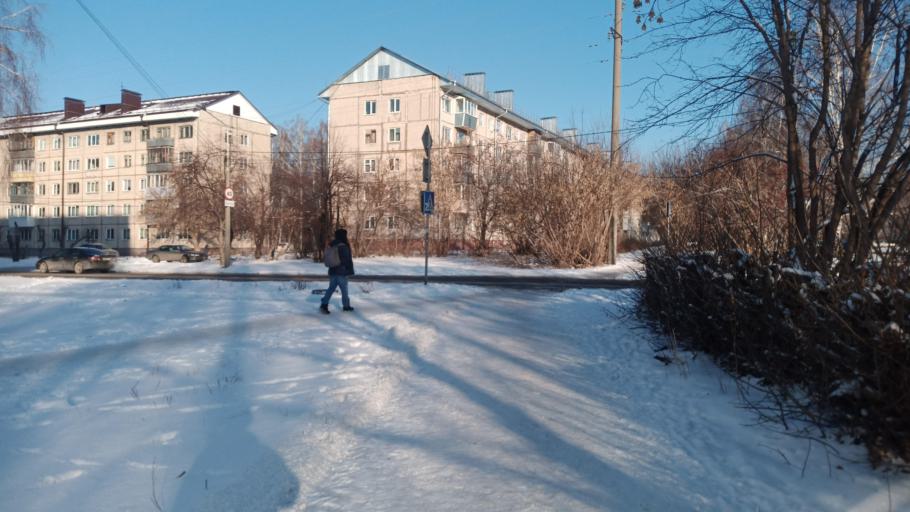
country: RU
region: Altai Krai
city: Yuzhnyy
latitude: 53.2494
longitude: 83.6886
